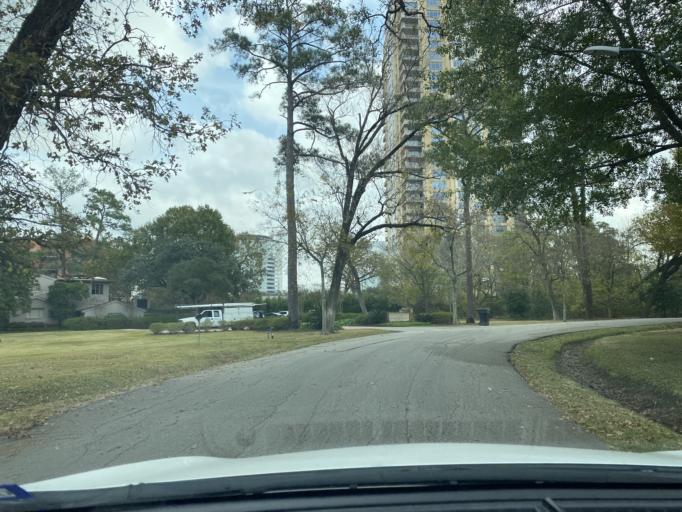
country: US
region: Texas
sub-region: Harris County
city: Hunters Creek Village
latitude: 29.7569
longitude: -95.4601
